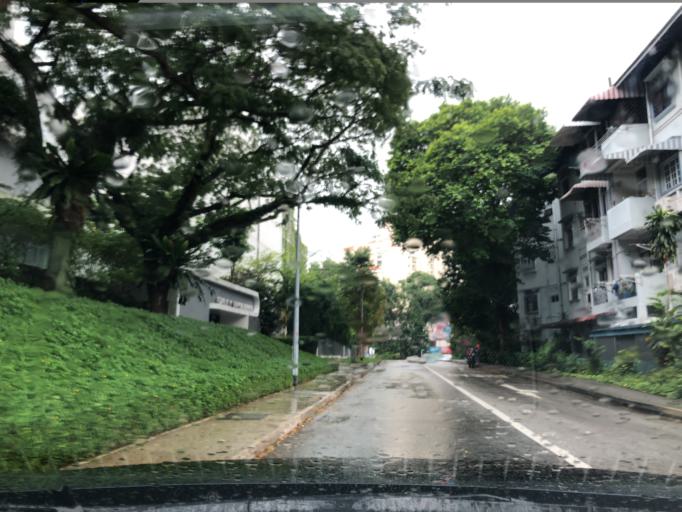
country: SG
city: Singapore
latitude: 1.2973
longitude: 103.8408
